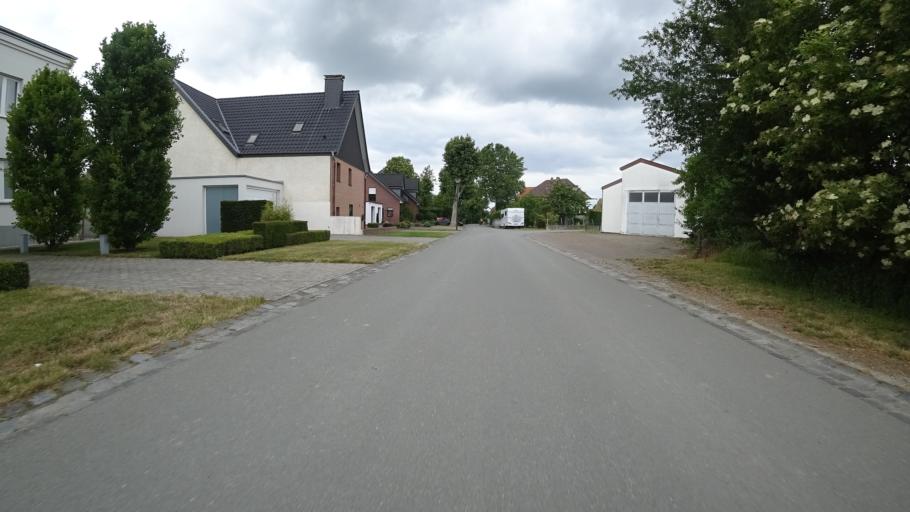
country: DE
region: North Rhine-Westphalia
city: Erwitte
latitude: 51.6263
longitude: 8.3698
